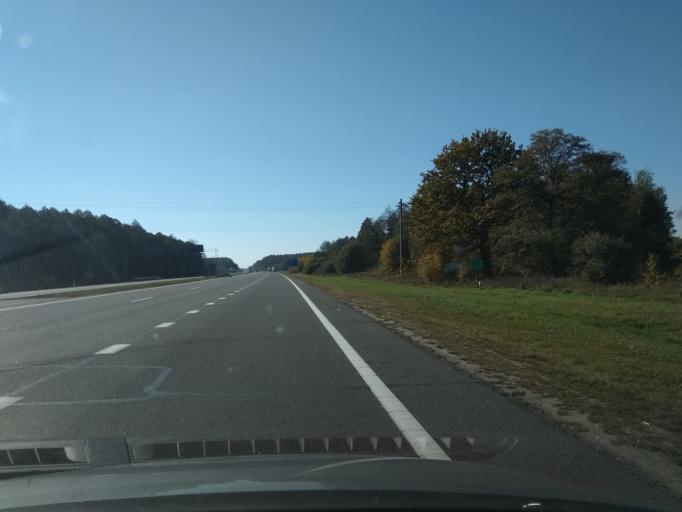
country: BY
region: Brest
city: Ivatsevichy
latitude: 52.6975
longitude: 25.3584
